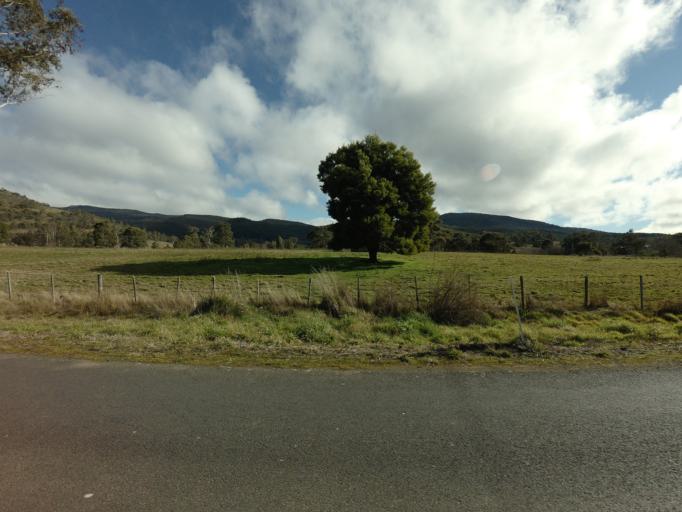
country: AU
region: Tasmania
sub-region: Derwent Valley
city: New Norfolk
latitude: -42.6030
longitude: 146.7061
